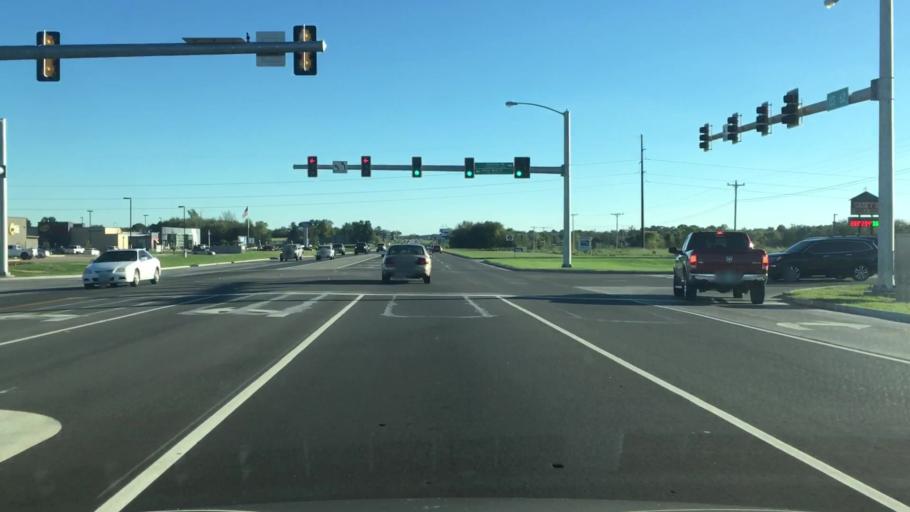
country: US
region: Oklahoma
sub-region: Cherokee County
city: Park Hill
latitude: 35.8776
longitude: -94.9763
